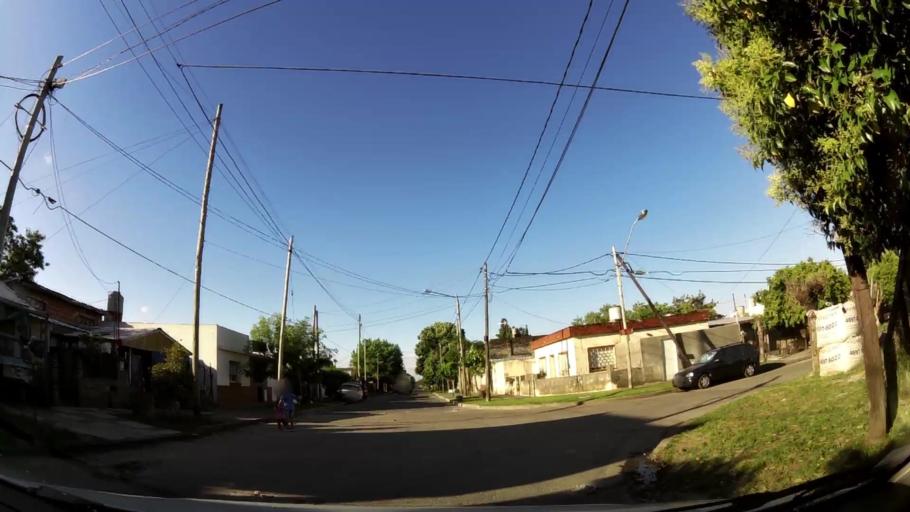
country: AR
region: Buenos Aires
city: Ituzaingo
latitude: -34.6850
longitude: -58.6414
